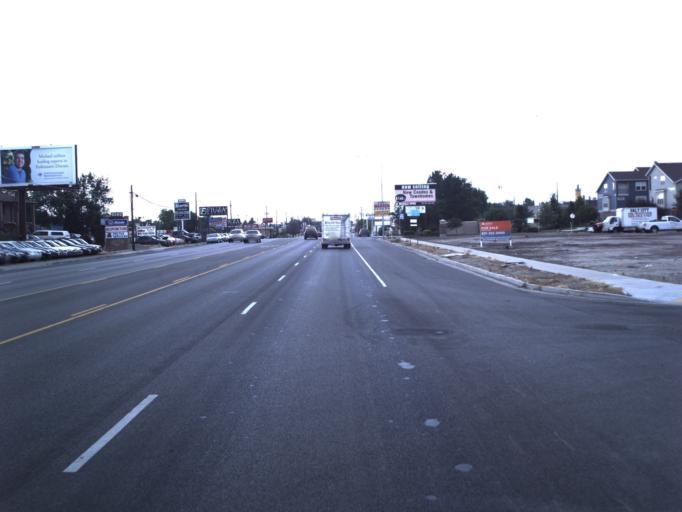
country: US
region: Utah
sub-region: Salt Lake County
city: Sandy City
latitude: 40.6002
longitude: -111.8907
